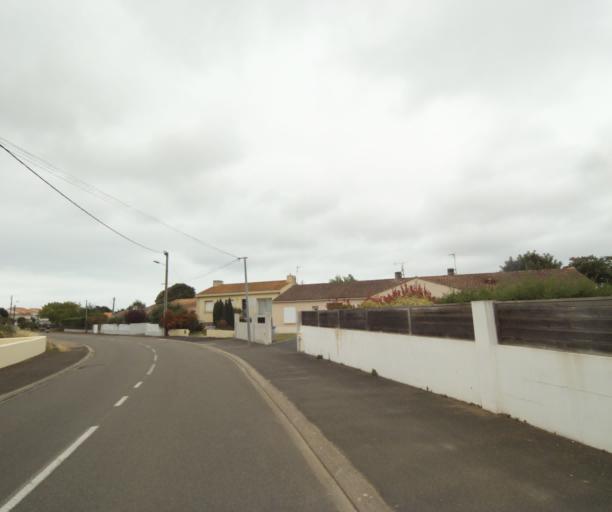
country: FR
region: Pays de la Loire
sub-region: Departement de la Vendee
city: Chateau-d'Olonne
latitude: 46.5034
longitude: -1.7496
